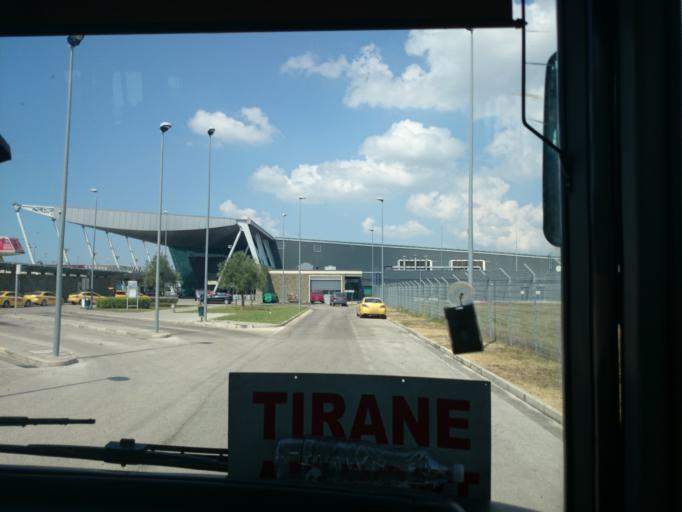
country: AL
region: Tirane
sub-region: Rrethi i Tiranes
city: Preze
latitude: 41.4176
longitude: 19.7142
